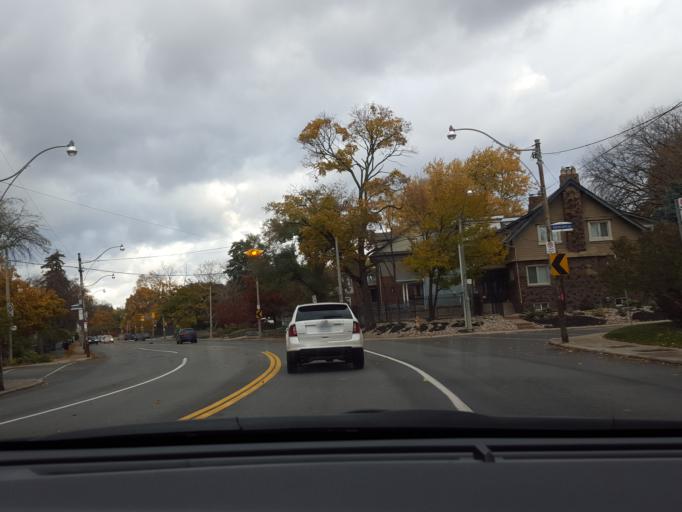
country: CA
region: Ontario
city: Toronto
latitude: 43.7157
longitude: -79.4121
